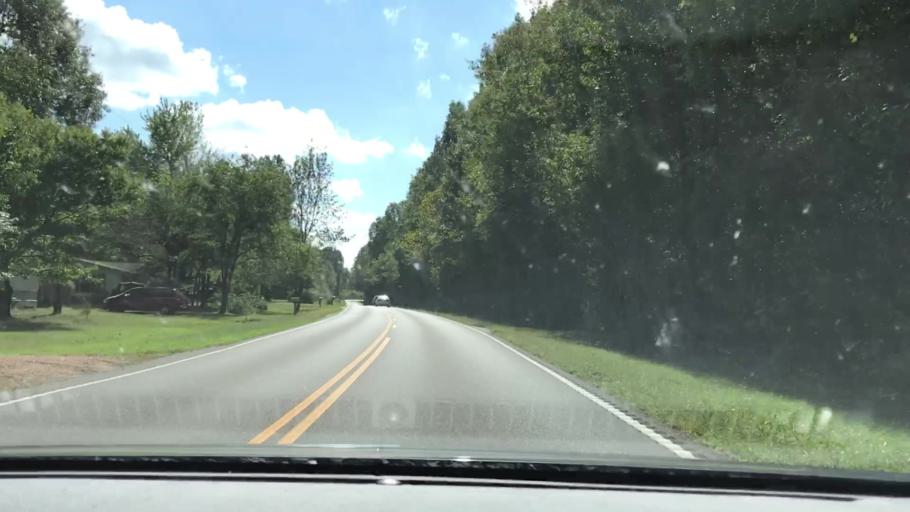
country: US
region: Kentucky
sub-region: McCracken County
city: Reidland
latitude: 36.9676
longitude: -88.5154
